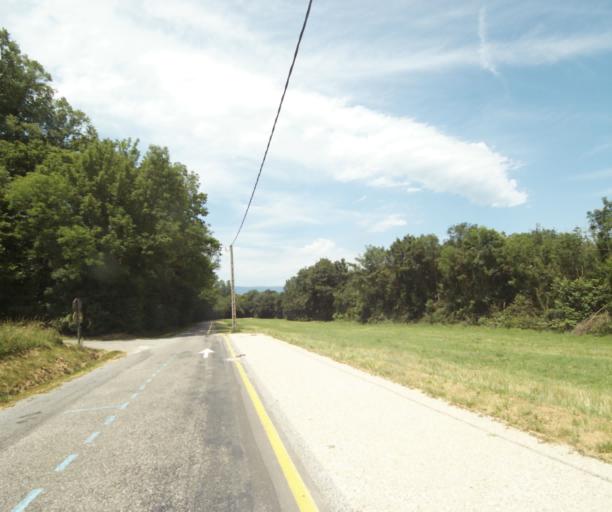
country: FR
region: Rhone-Alpes
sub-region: Departement de la Haute-Savoie
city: Chens-sur-Leman
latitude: 46.3199
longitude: 6.2645
